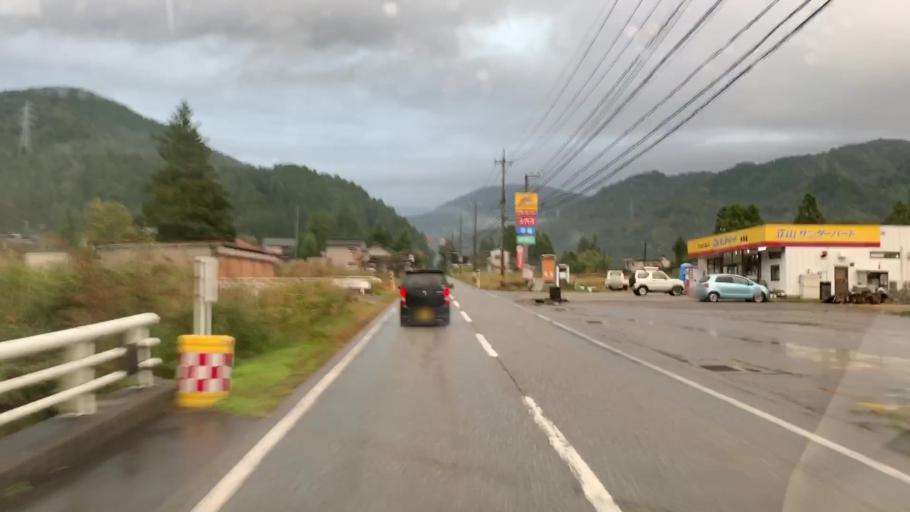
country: JP
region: Toyama
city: Kamiichi
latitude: 36.5850
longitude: 137.3338
